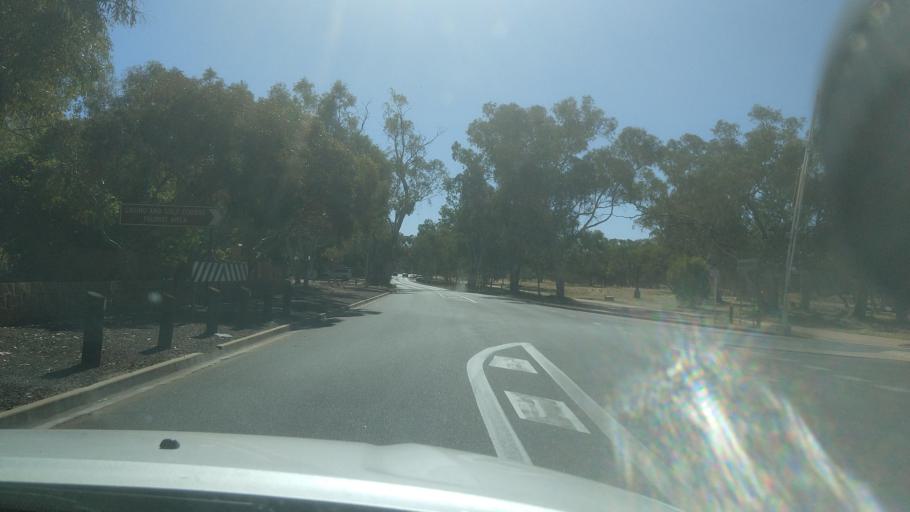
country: AU
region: Northern Territory
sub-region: Alice Springs
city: Alice Springs
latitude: -23.7205
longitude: 133.8735
